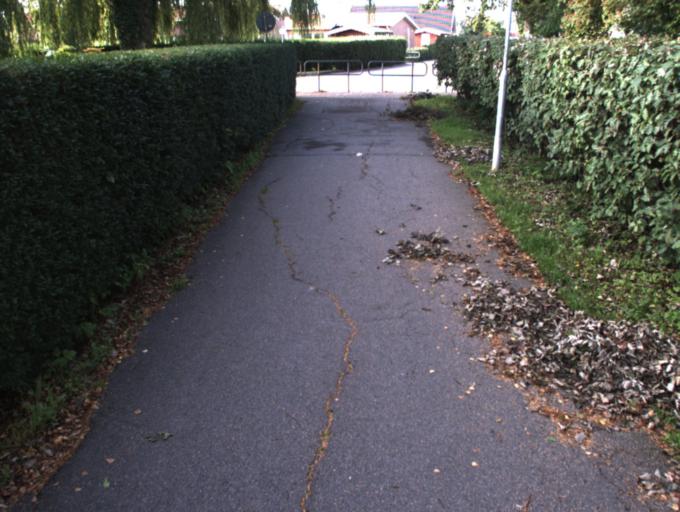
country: SE
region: Skane
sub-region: Angelholms Kommun
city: Strovelstorp
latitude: 56.1410
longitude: 12.7814
